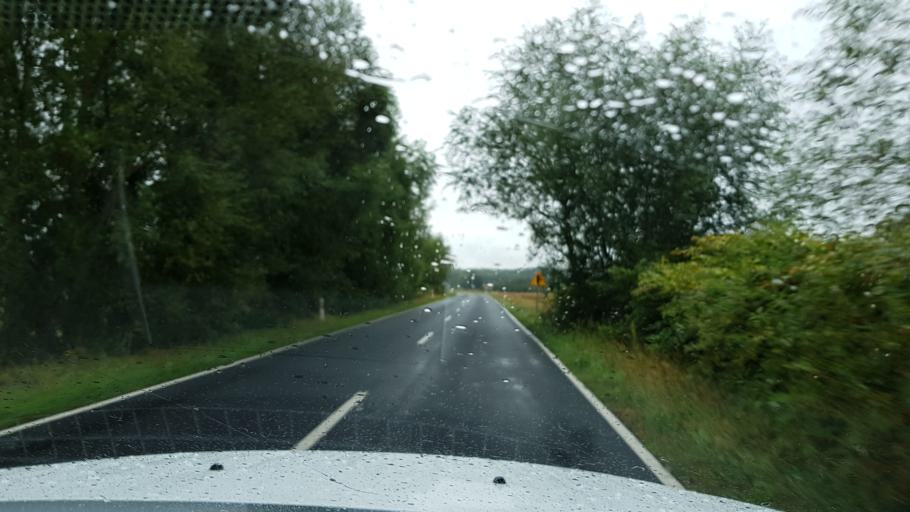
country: PL
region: West Pomeranian Voivodeship
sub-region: Powiat gryfinski
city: Widuchowa
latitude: 53.0797
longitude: 14.3755
